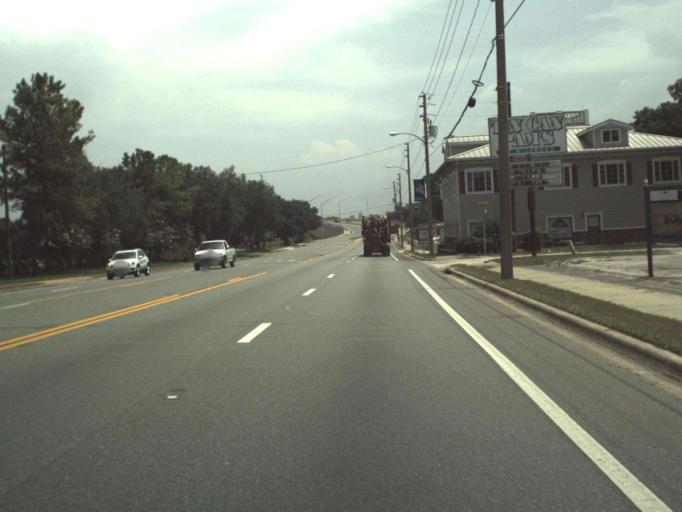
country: US
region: Florida
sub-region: Sumter County
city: Wildwood
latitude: 28.8684
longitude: -82.0382
